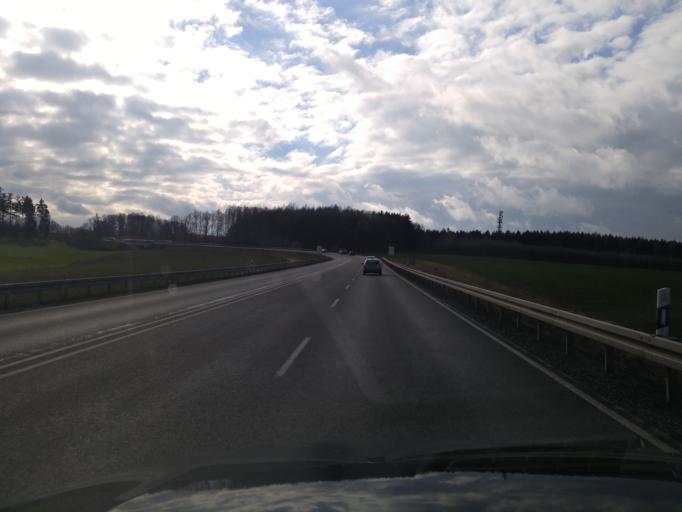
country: DE
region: Saxony
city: Hirschfeld
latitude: 50.6443
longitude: 12.4415
